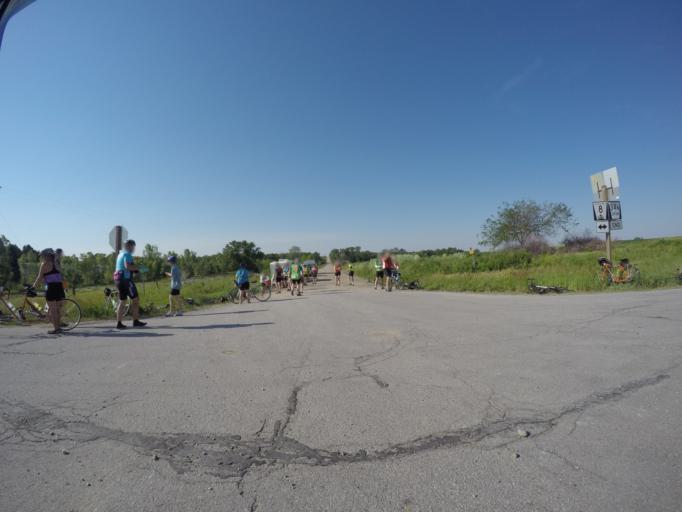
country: US
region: Nebraska
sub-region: Gage County
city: Wymore
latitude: 40.0446
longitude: -96.4829
